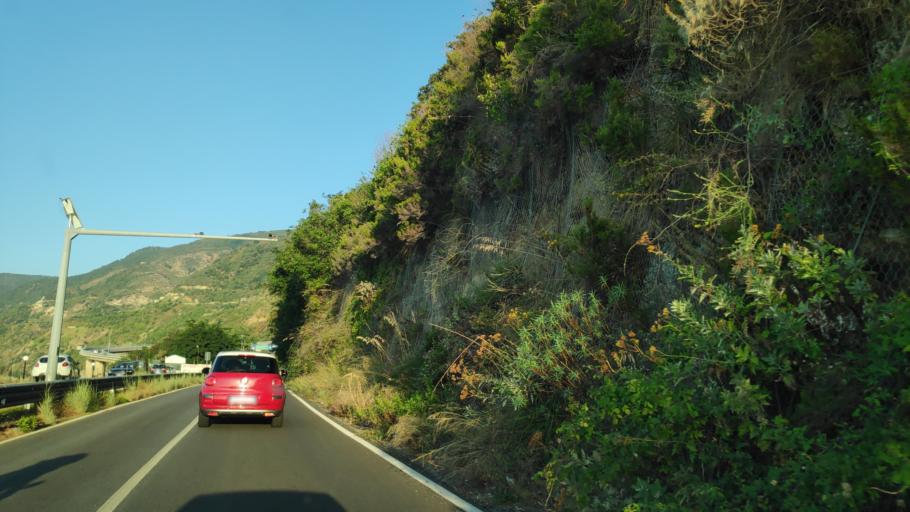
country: IT
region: Calabria
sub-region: Provincia di Reggio Calabria
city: Scilla
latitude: 38.2534
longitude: 15.7223
